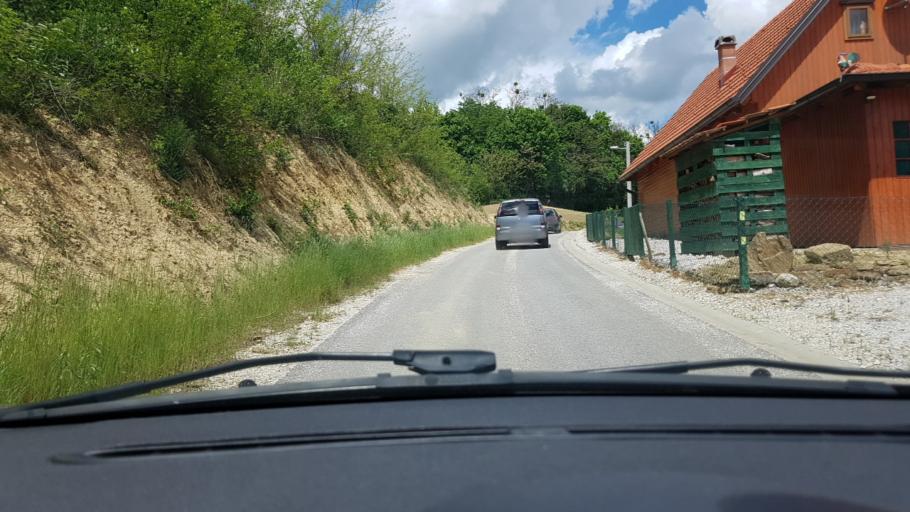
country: HR
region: Krapinsko-Zagorska
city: Pregrada
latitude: 46.1649
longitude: 15.8105
